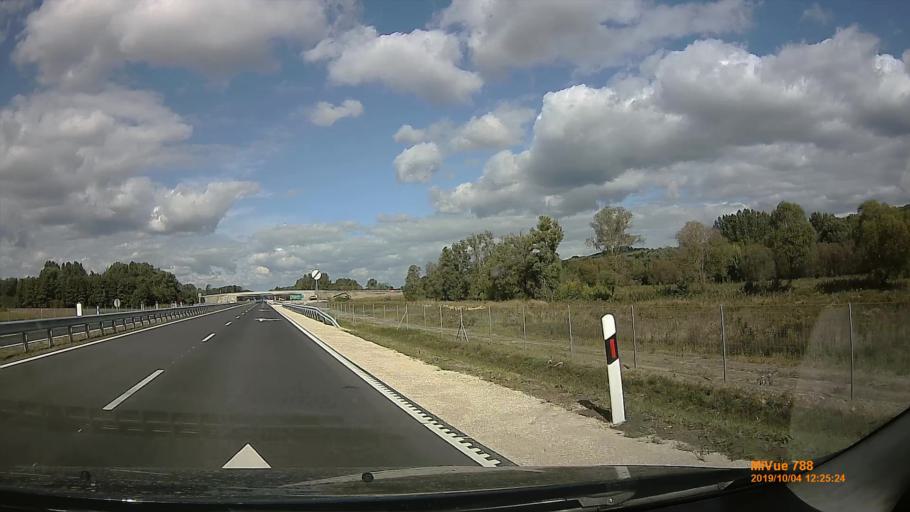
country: HU
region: Somogy
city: Karad
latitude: 46.6629
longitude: 17.7844
